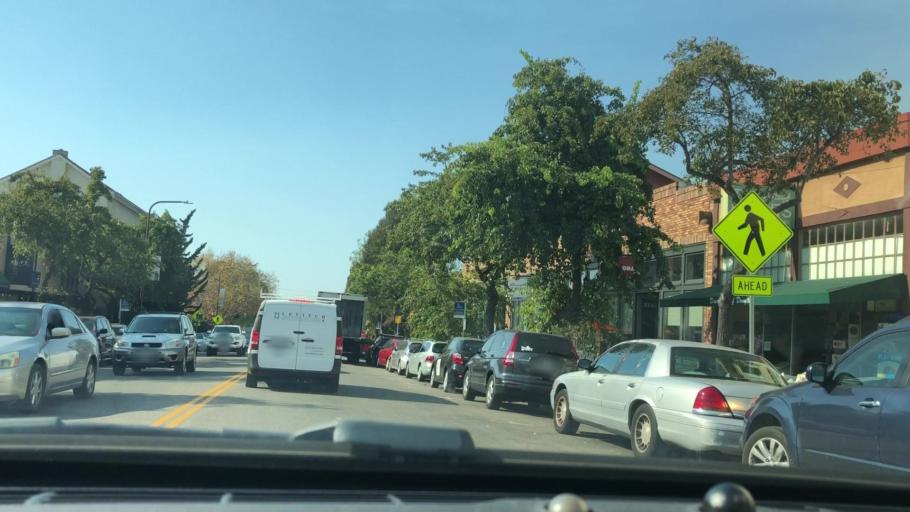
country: US
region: California
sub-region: Alameda County
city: Berkeley
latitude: 37.8571
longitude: -122.2531
